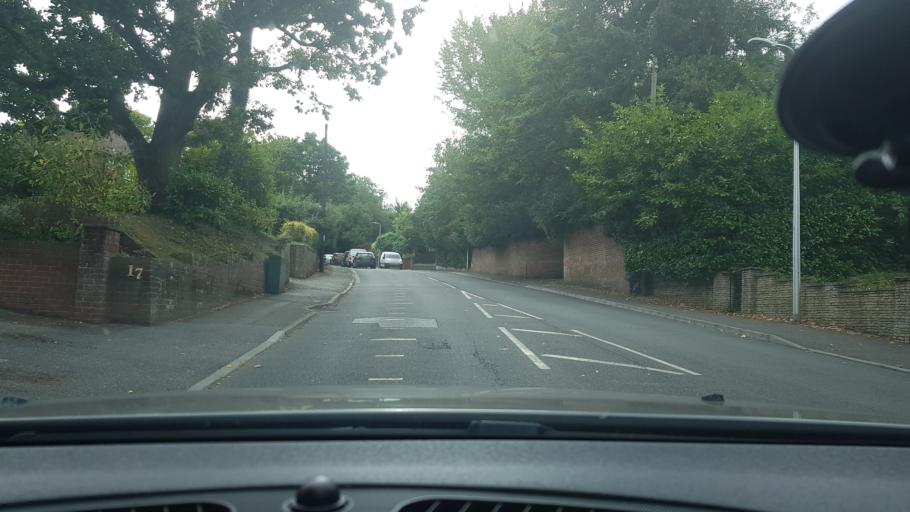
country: GB
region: England
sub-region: West Berkshire
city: Greenham
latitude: 51.3913
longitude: -1.3144
